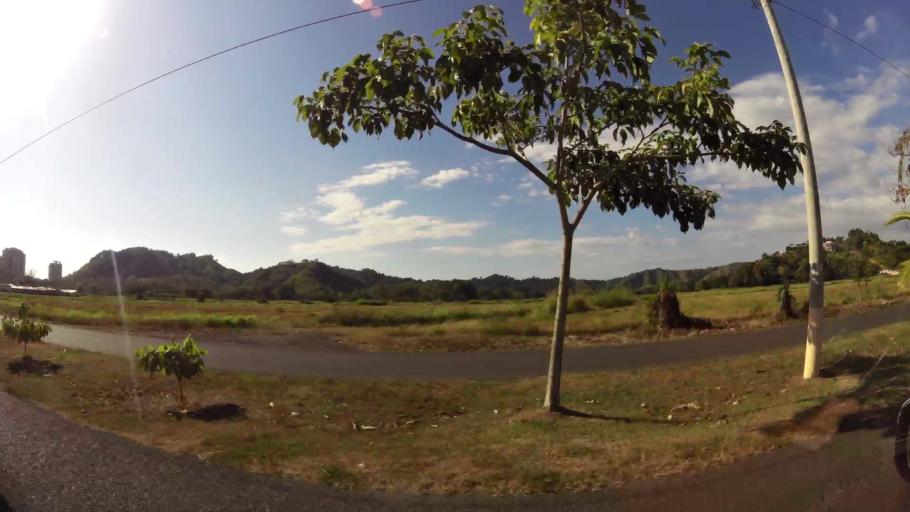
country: CR
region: Puntarenas
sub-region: Canton de Garabito
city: Jaco
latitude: 9.6263
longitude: -84.6339
